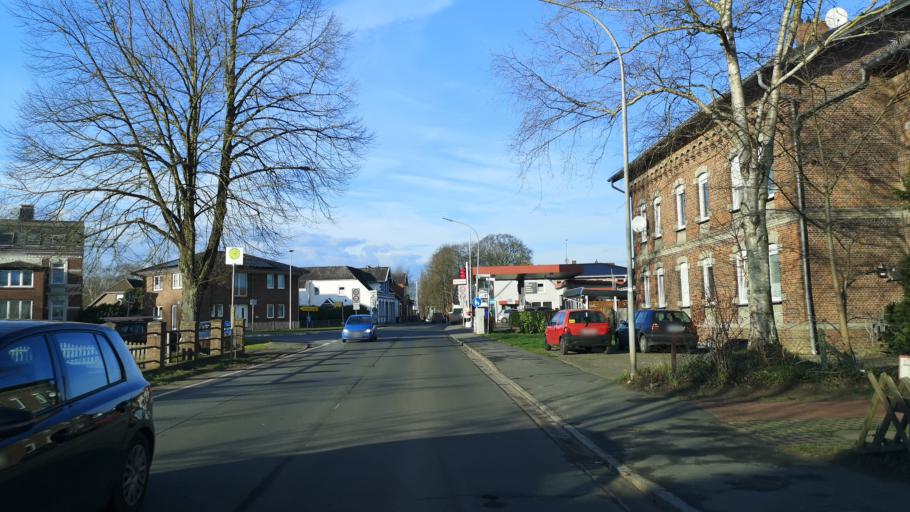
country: DE
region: Schleswig-Holstein
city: Lagerdorf
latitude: 53.8845
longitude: 9.5794
